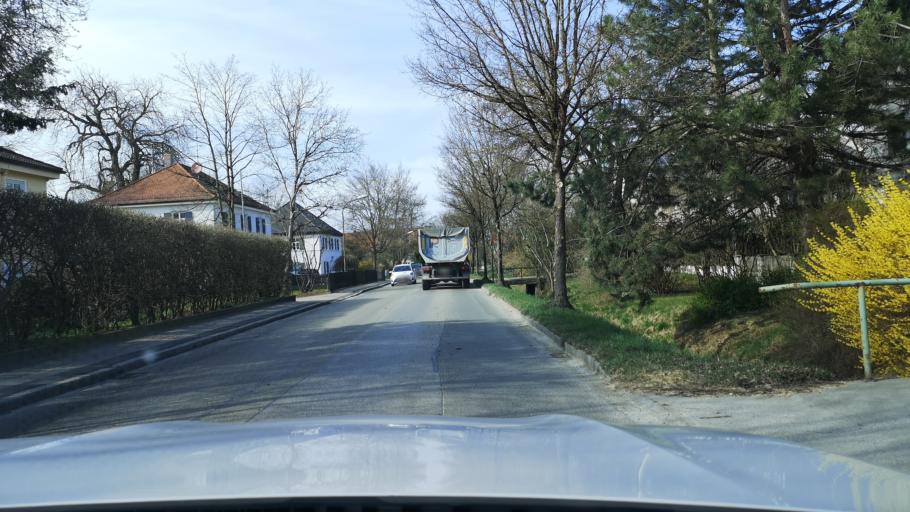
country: DE
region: Bavaria
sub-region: Upper Bavaria
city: Pastetten
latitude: 48.2015
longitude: 11.9629
